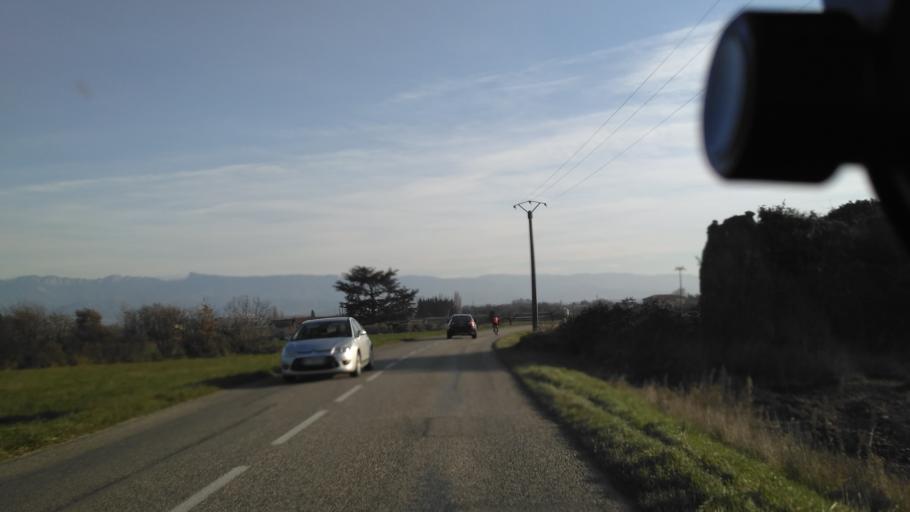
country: FR
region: Rhone-Alpes
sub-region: Departement de la Drome
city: Alixan
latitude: 44.9960
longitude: 5.0019
